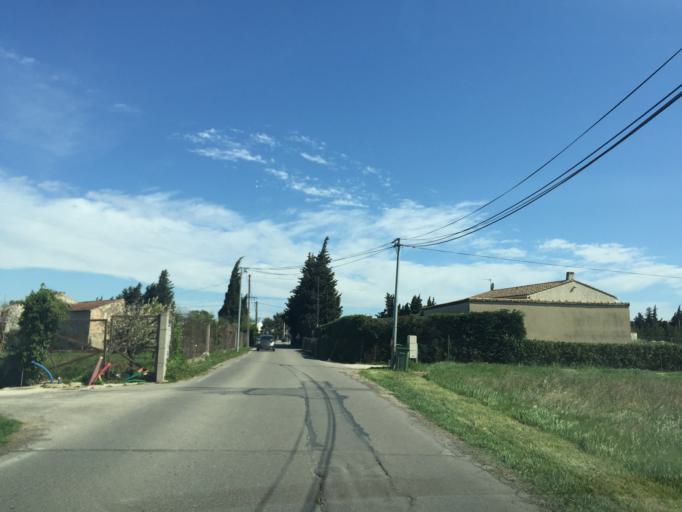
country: FR
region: Provence-Alpes-Cote d'Azur
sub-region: Departement du Vaucluse
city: Sorgues
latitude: 43.9943
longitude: 4.8832
